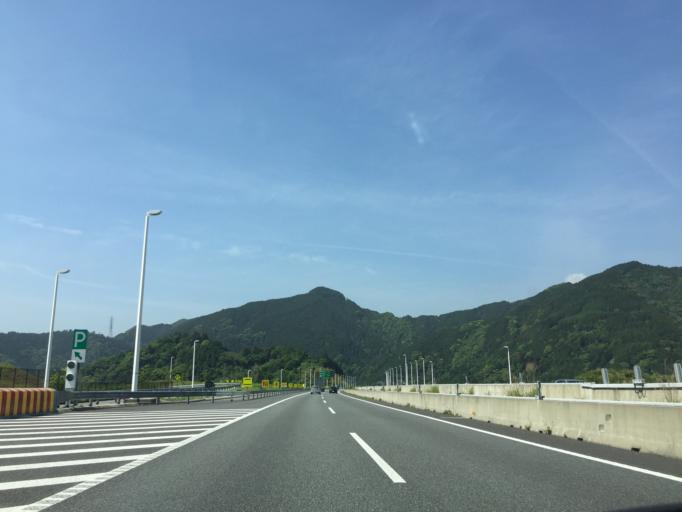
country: JP
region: Shizuoka
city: Fujinomiya
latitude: 35.1330
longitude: 138.5110
